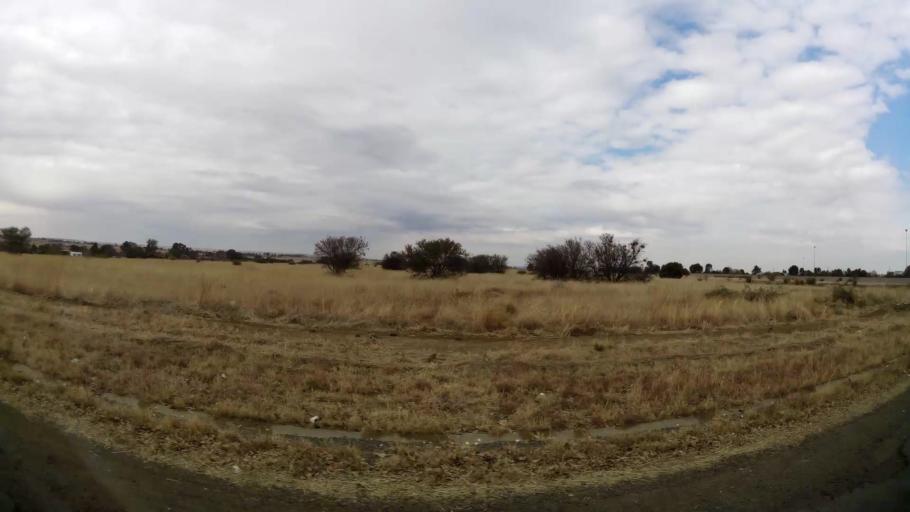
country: ZA
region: Orange Free State
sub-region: Fezile Dabi District Municipality
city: Kroonstad
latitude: -27.6345
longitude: 27.2439
